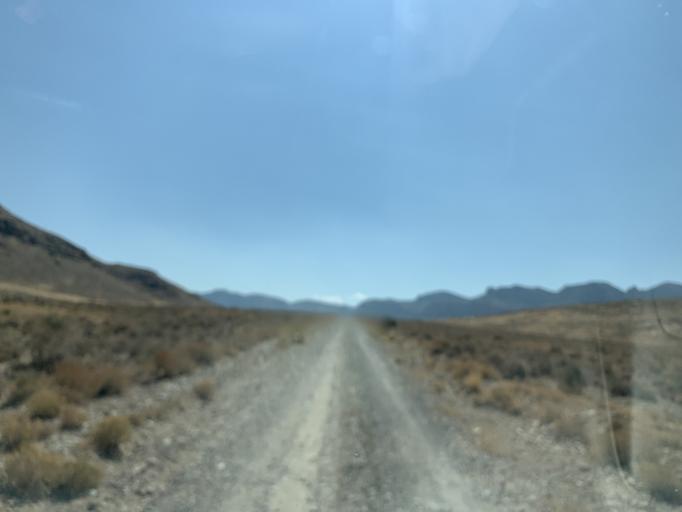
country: US
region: Utah
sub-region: Beaver County
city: Milford
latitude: 38.9789
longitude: -113.4490
